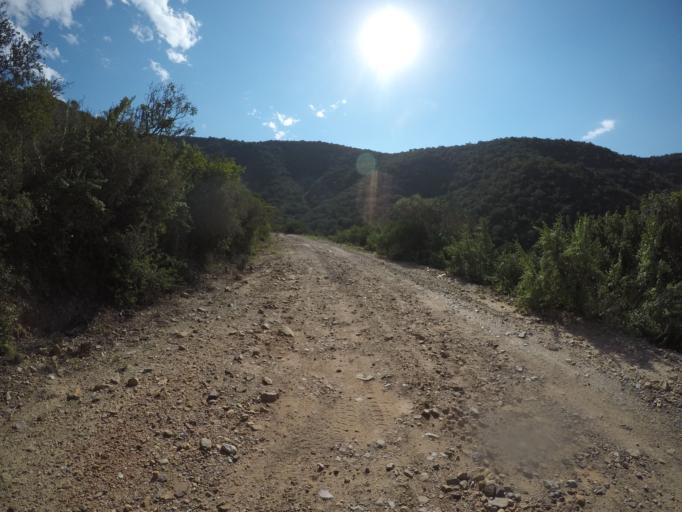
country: ZA
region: Eastern Cape
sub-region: Cacadu District Municipality
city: Kareedouw
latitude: -33.6523
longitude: 24.3483
